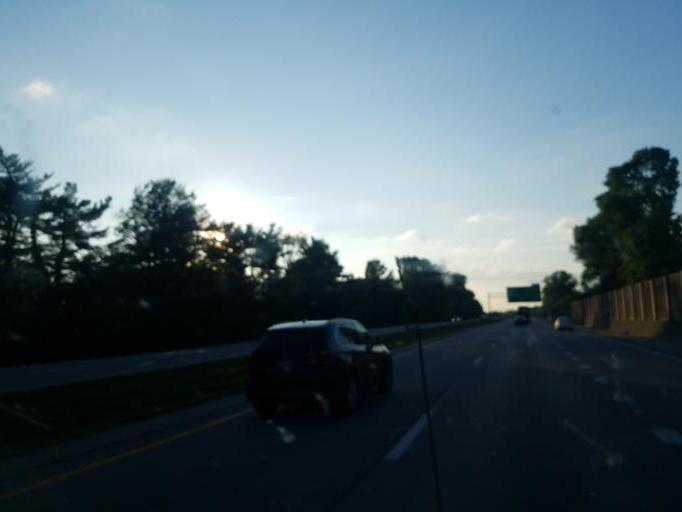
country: US
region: Kentucky
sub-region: Jefferson County
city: Windy Hills
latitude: 38.2725
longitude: -85.6290
